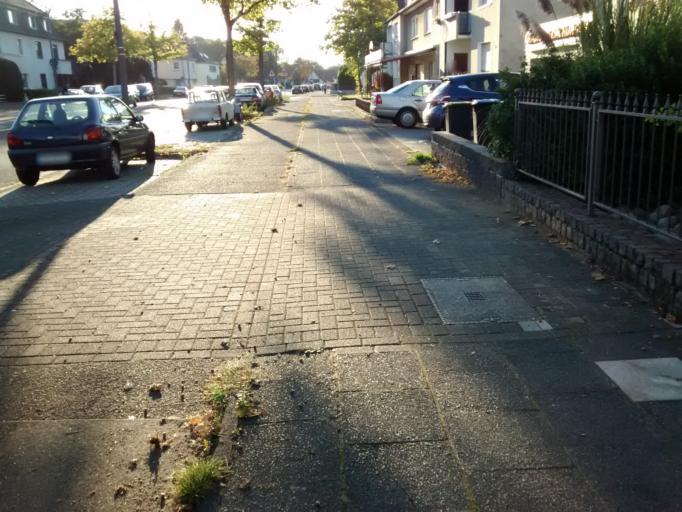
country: DE
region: North Rhine-Westphalia
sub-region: Regierungsbezirk Koln
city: Muelheim
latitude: 50.9967
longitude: 7.0409
